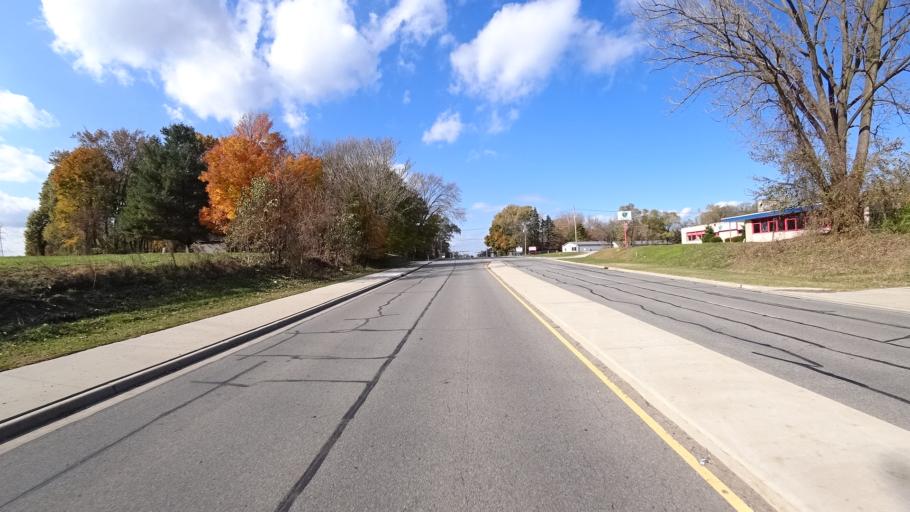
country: US
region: Indiana
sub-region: LaPorte County
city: Trail Creek
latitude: 41.7066
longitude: -86.8612
